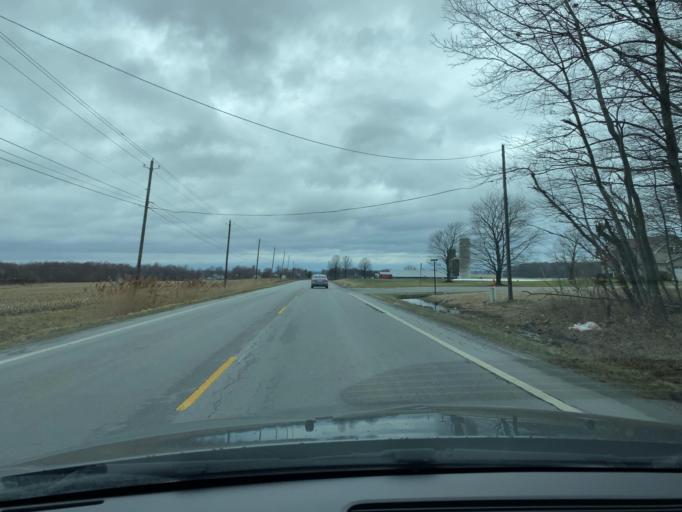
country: US
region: Ohio
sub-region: Wayne County
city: Orrville
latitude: 40.8879
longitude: -81.7631
